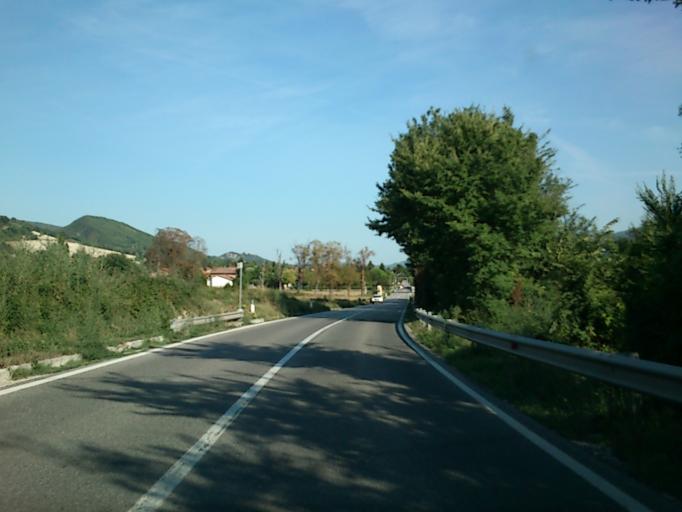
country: IT
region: The Marches
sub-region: Provincia di Pesaro e Urbino
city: Canavaccio
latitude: 43.6979
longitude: 12.6912
